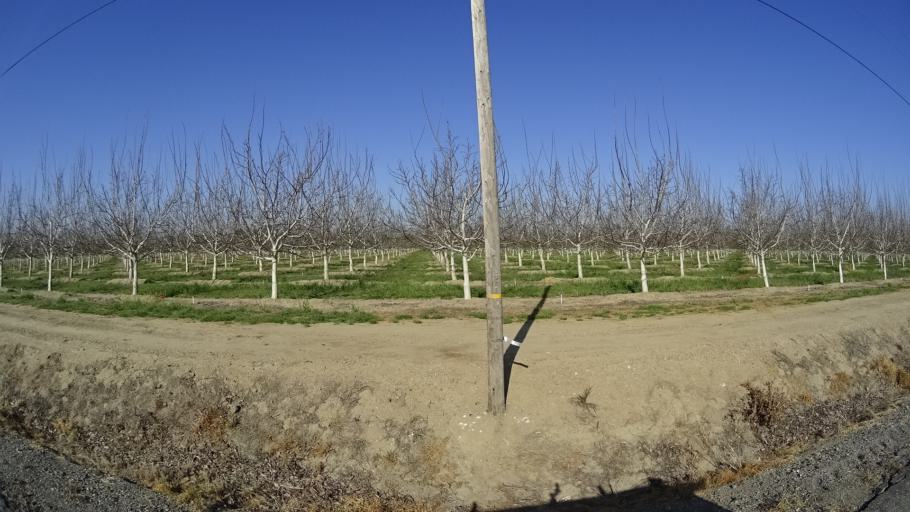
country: US
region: California
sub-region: Glenn County
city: Willows
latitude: 39.5765
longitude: -122.1170
